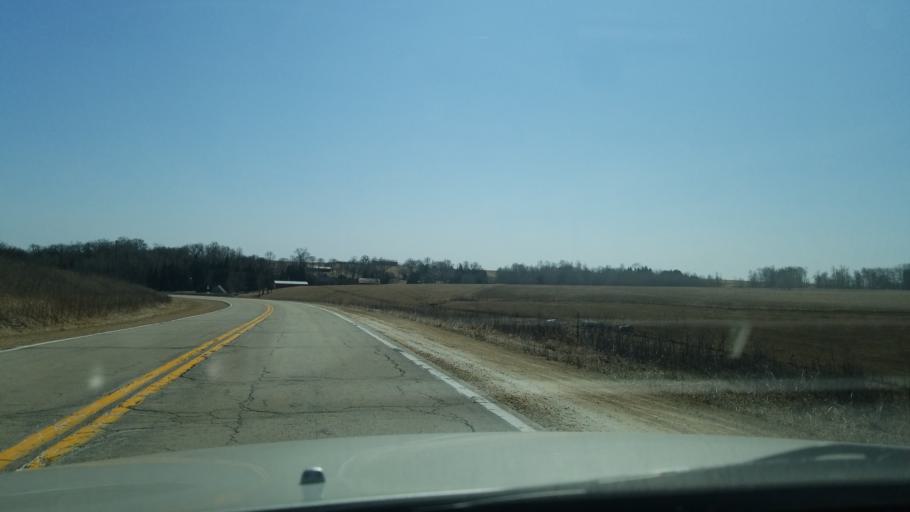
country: US
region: Wisconsin
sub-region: Iowa County
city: Mineral Point
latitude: 42.8859
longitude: -90.2260
